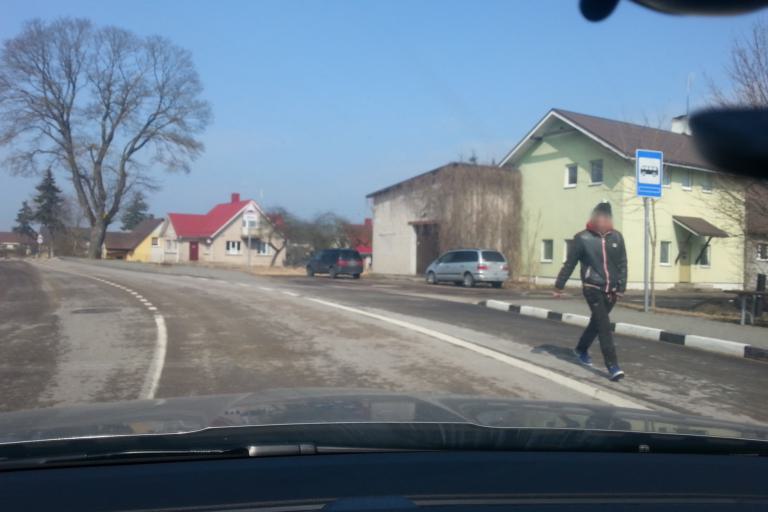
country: LT
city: Trakai
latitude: 54.6064
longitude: 24.9850
